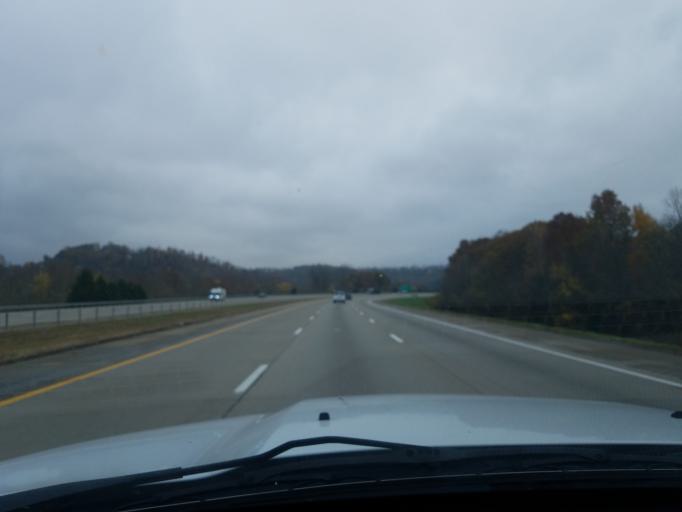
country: US
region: Kentucky
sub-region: Bullitt County
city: Lebanon Junction
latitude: 37.7935
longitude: -85.7549
